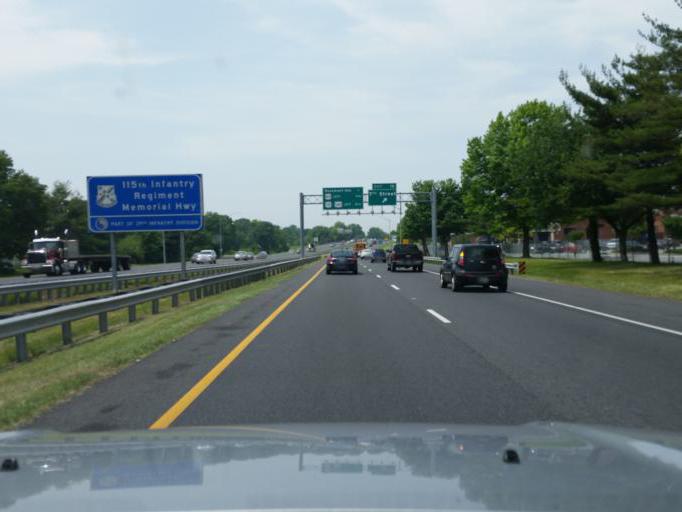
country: US
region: Maryland
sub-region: Frederick County
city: Frederick
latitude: 39.4323
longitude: -77.4148
